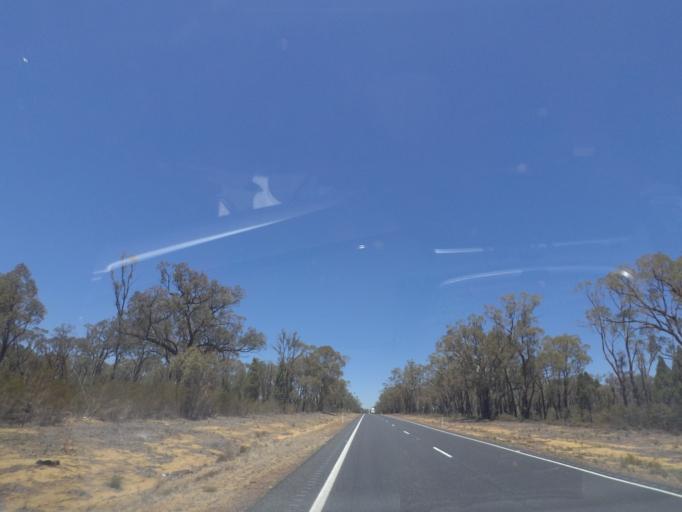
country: AU
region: New South Wales
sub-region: Narrabri
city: Narrabri
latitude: -30.7424
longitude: 149.5148
